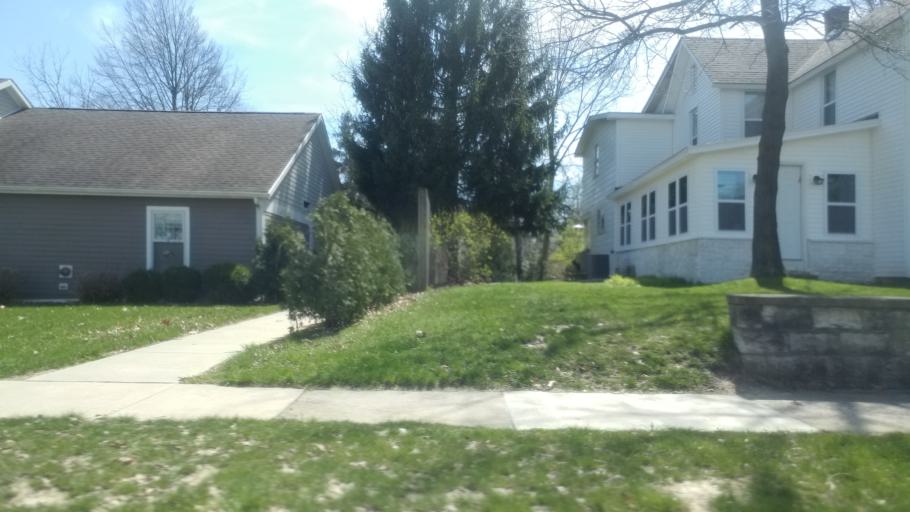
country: US
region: Ohio
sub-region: Wood County
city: Bowling Green
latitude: 41.3787
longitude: -83.6579
